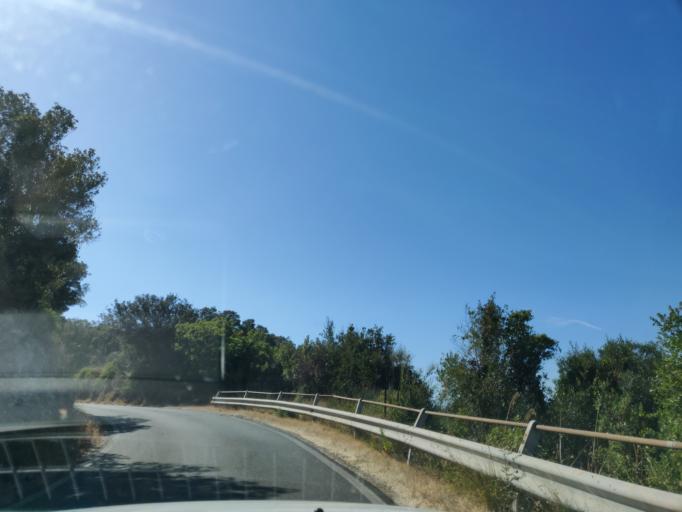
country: IT
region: Tuscany
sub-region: Provincia di Grosseto
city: Porto Ercole
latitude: 42.4325
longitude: 11.1734
